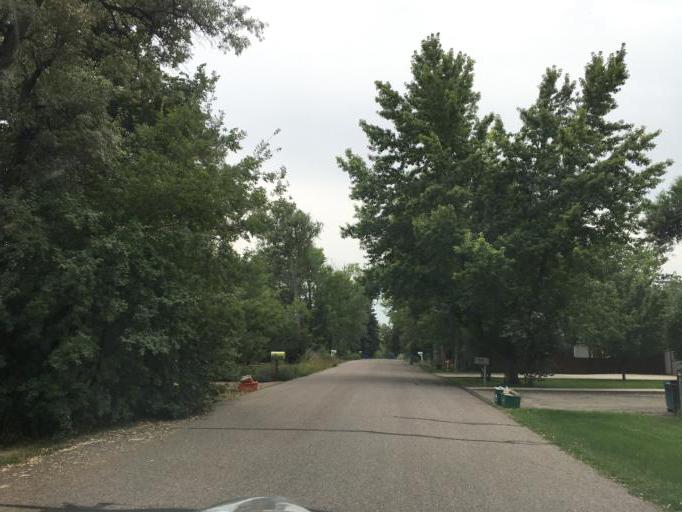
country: US
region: Colorado
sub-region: Jefferson County
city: Wheat Ridge
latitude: 39.7508
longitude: -105.0920
